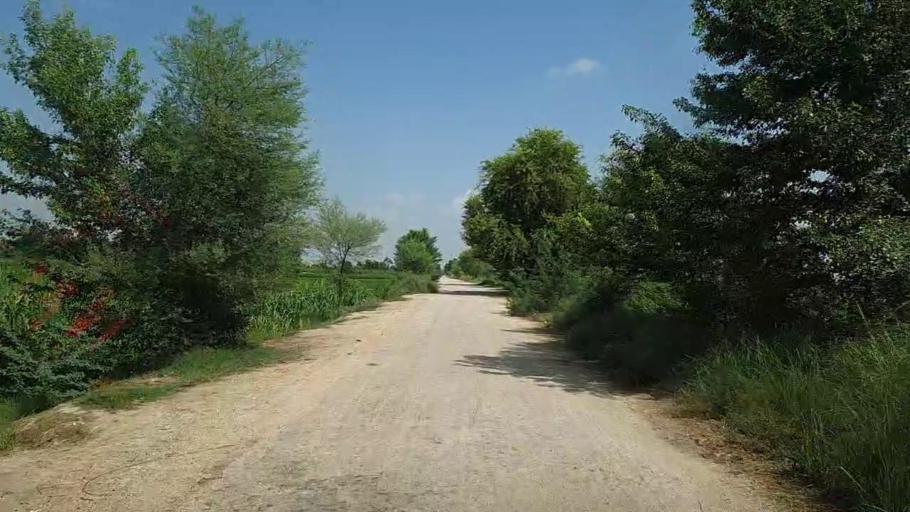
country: PK
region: Sindh
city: Bhiria
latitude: 26.8752
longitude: 68.2490
